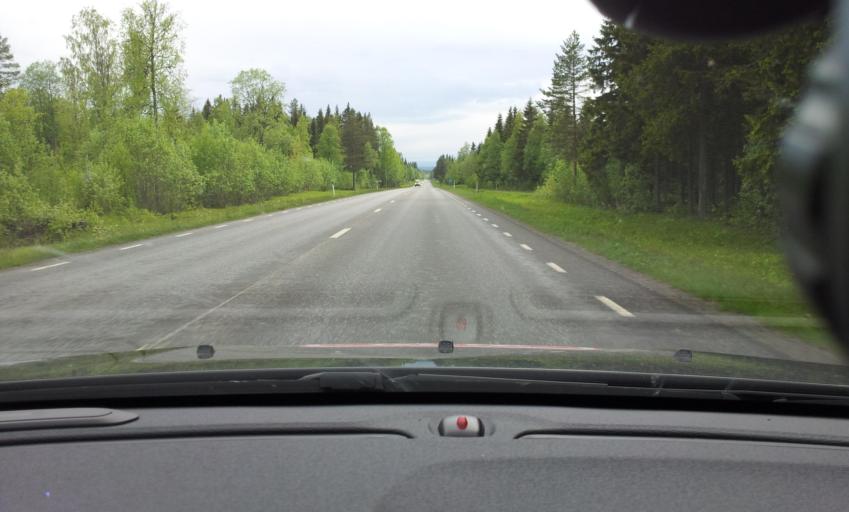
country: SE
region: Jaemtland
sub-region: OEstersunds Kommun
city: Ostersund
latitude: 63.1927
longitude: 14.7577
